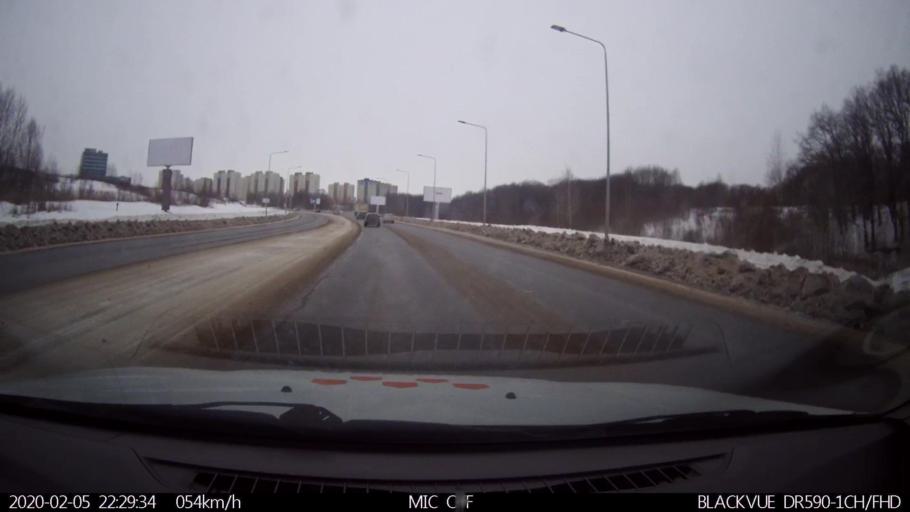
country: RU
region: Nizjnij Novgorod
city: Imeni Stepana Razina
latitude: 54.7484
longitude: 44.1461
